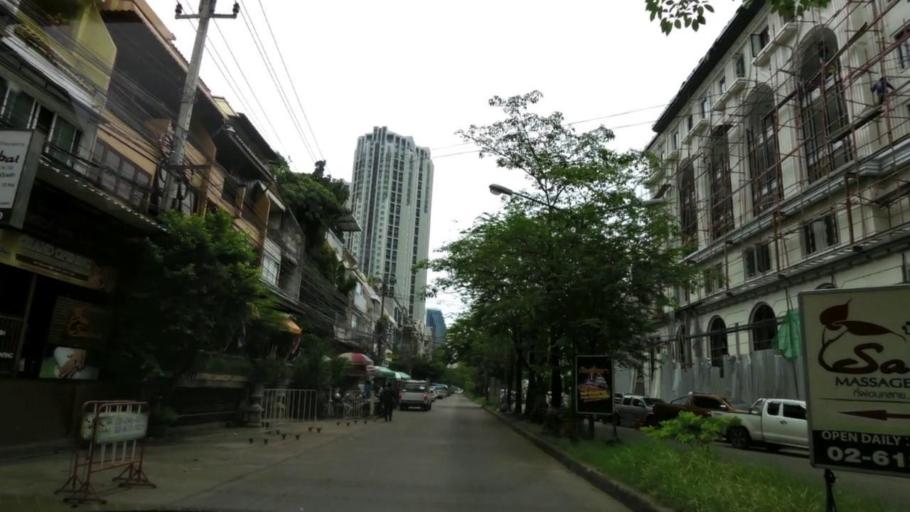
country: TH
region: Bangkok
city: Din Daeng
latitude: 13.7573
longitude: 100.5700
